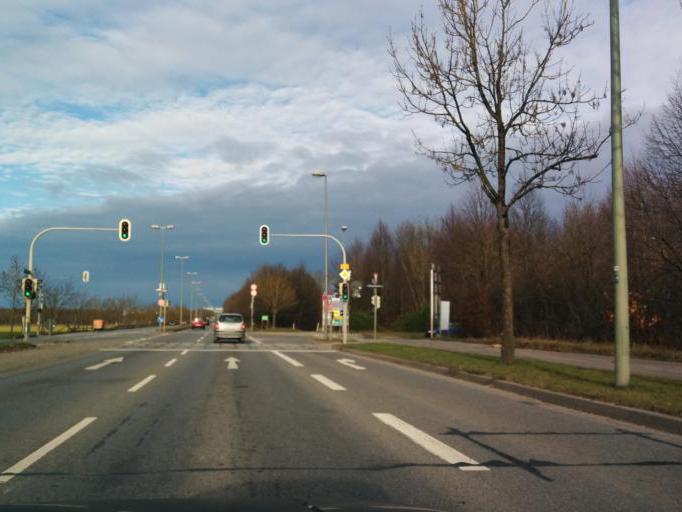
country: DE
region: Bavaria
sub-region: Upper Bavaria
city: Karlsfeld
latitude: 48.2012
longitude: 11.4919
